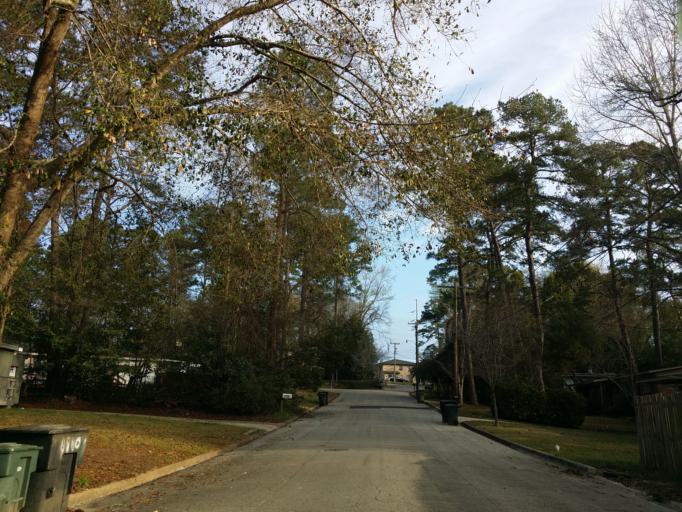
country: US
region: Florida
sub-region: Leon County
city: Tallahassee
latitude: 30.4554
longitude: -84.2535
